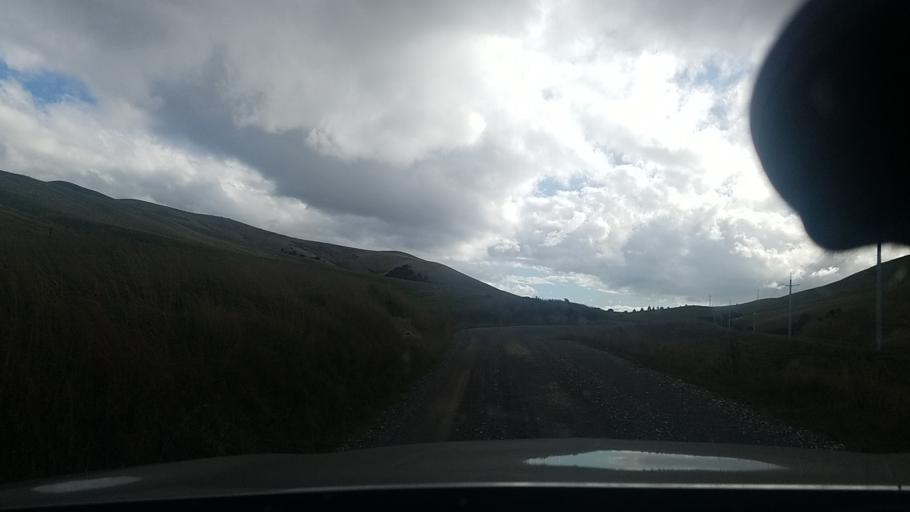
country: NZ
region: Marlborough
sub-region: Marlborough District
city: Blenheim
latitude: -41.5865
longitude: 174.0862
